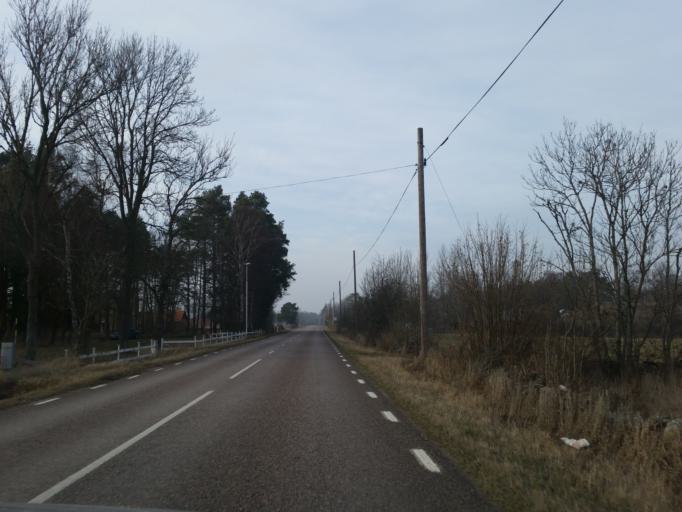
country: SE
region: Kalmar
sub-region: Borgholms Kommun
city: Borgholm
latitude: 57.2042
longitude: 16.9781
